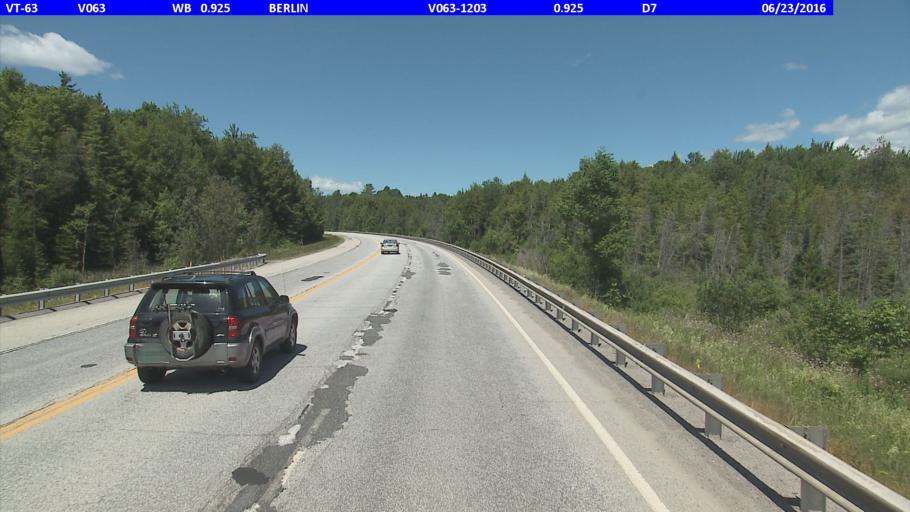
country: US
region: Vermont
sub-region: Orange County
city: Williamstown
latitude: 44.1666
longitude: -72.5595
